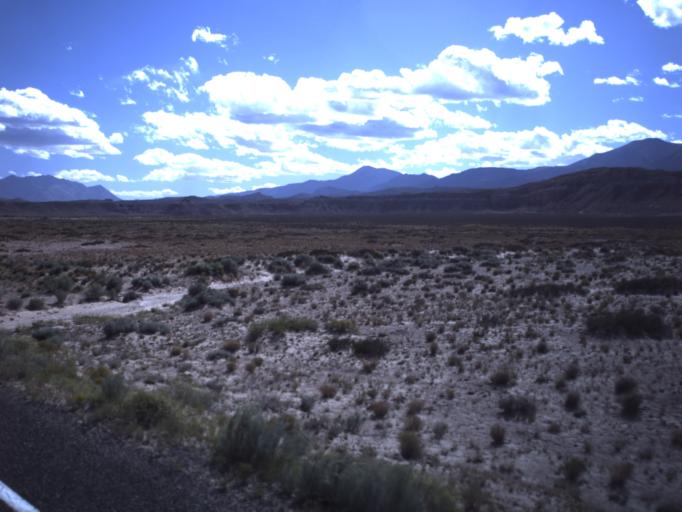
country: US
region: Utah
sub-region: Wayne County
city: Loa
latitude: 38.1782
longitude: -110.6255
